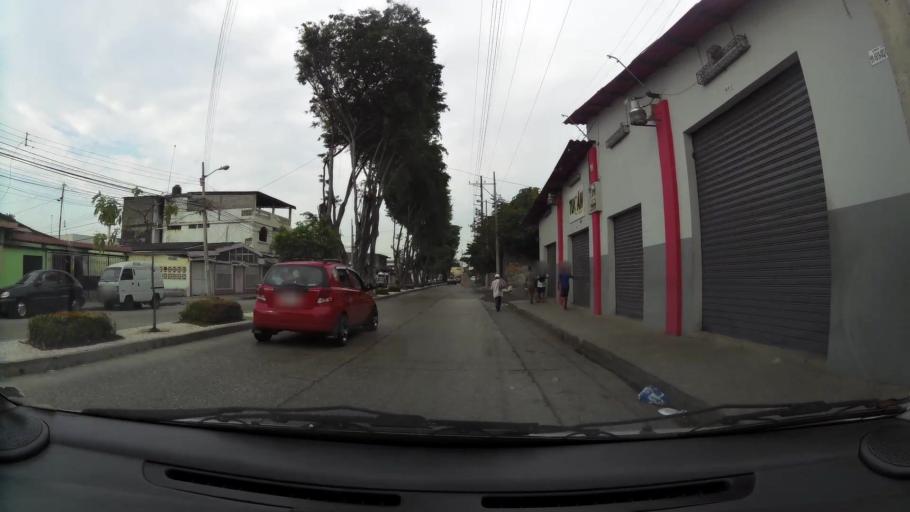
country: EC
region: Guayas
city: Guayaquil
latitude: -2.2465
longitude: -79.8967
